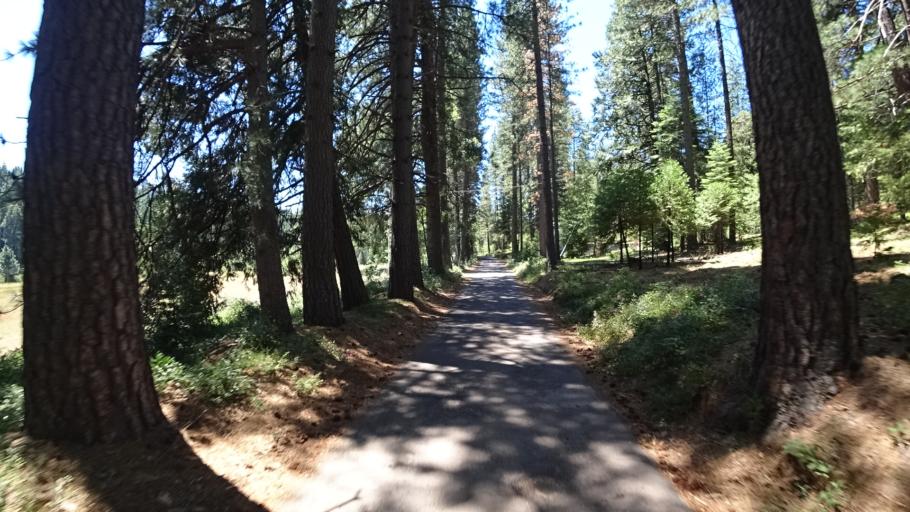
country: US
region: California
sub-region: Calaveras County
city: Arnold
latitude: 38.2268
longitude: -120.3267
